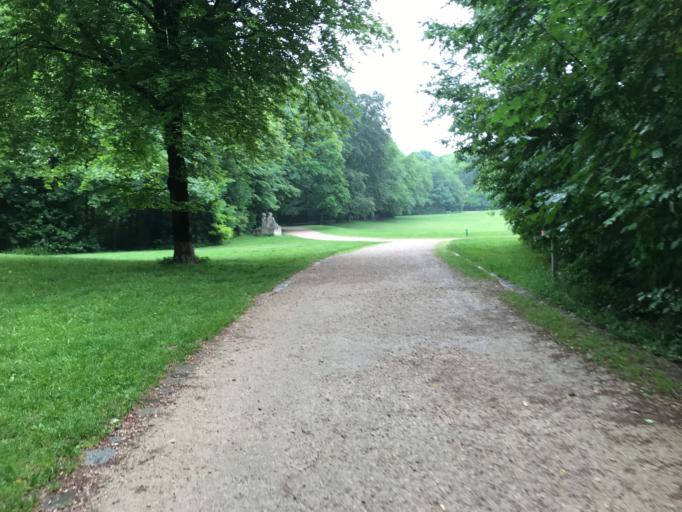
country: DE
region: Bavaria
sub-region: Upper Bavaria
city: Munich
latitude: 48.1316
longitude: 11.5414
